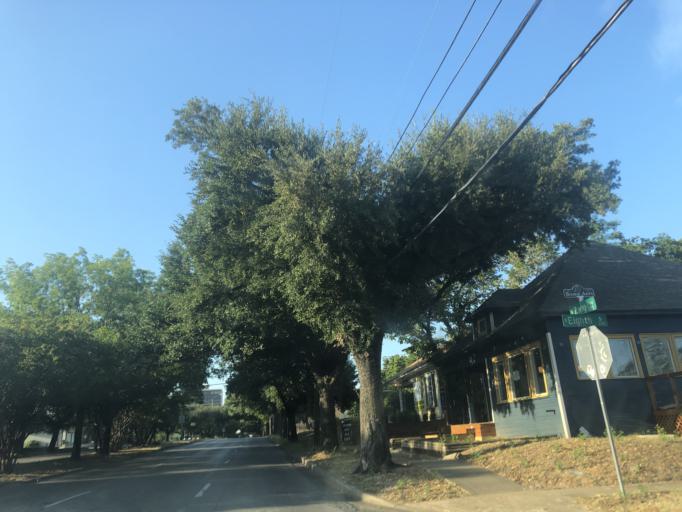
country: US
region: Texas
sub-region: Dallas County
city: Dallas
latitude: 32.7482
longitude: -96.8247
